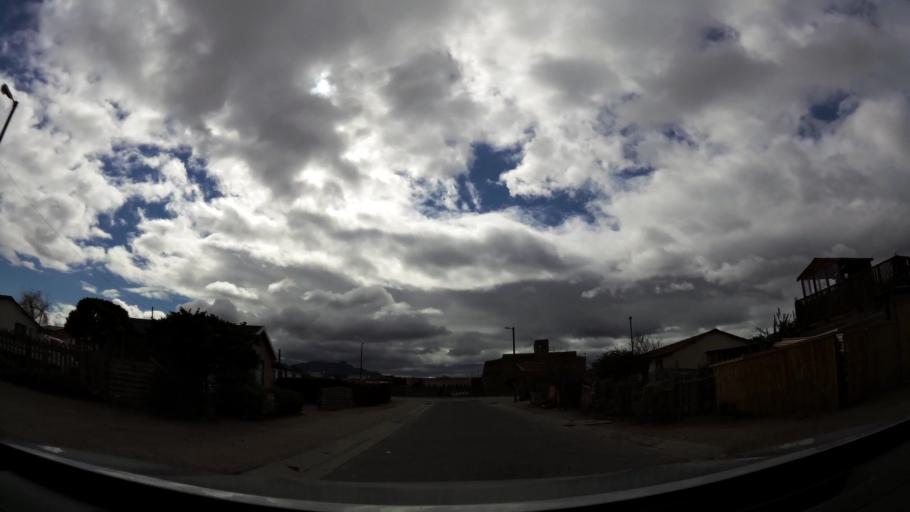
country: ZA
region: Western Cape
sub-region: Eden District Municipality
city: George
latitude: -34.0225
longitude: 22.4659
